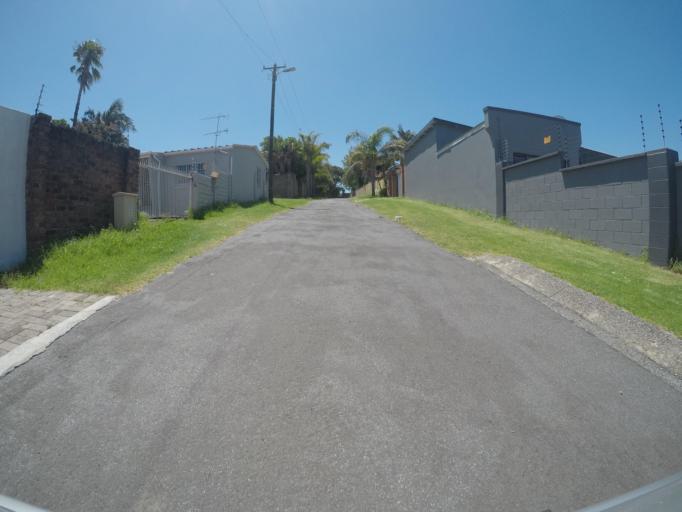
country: ZA
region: Eastern Cape
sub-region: Buffalo City Metropolitan Municipality
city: East London
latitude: -32.9893
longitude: 27.9049
